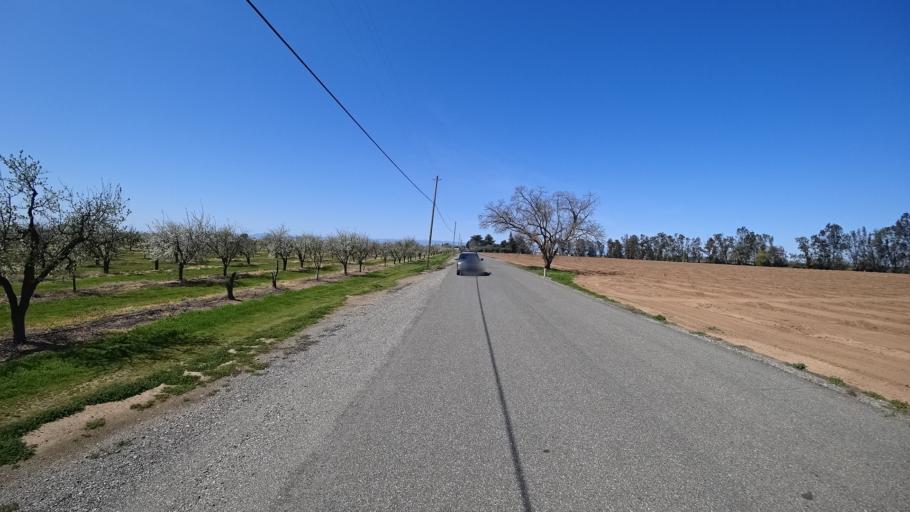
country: US
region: California
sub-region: Glenn County
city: Hamilton City
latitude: 39.7969
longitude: -122.0716
